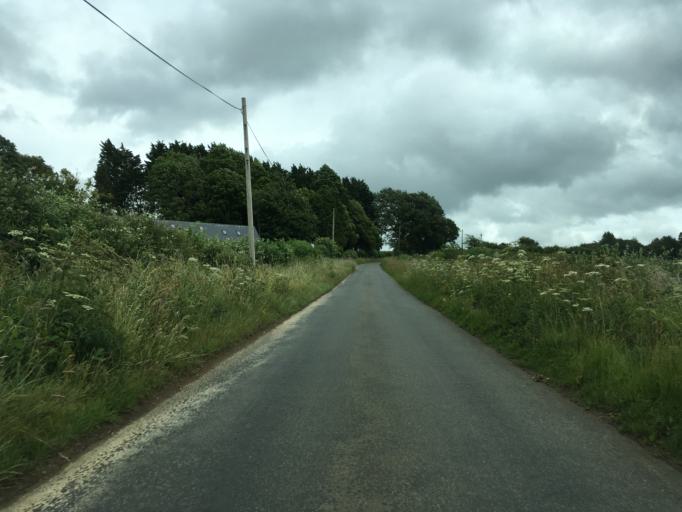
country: GB
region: England
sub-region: Gloucestershire
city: Mickleton
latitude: 52.0718
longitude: -1.7411
